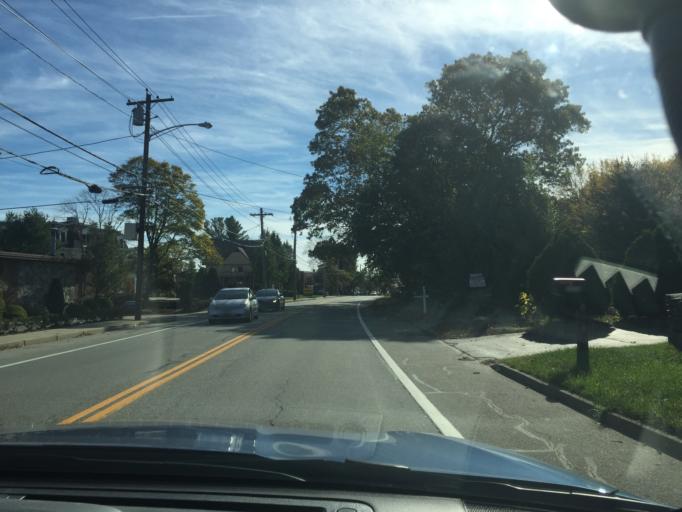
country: US
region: Rhode Island
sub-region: Kent County
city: East Greenwich
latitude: 41.6838
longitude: -71.4519
